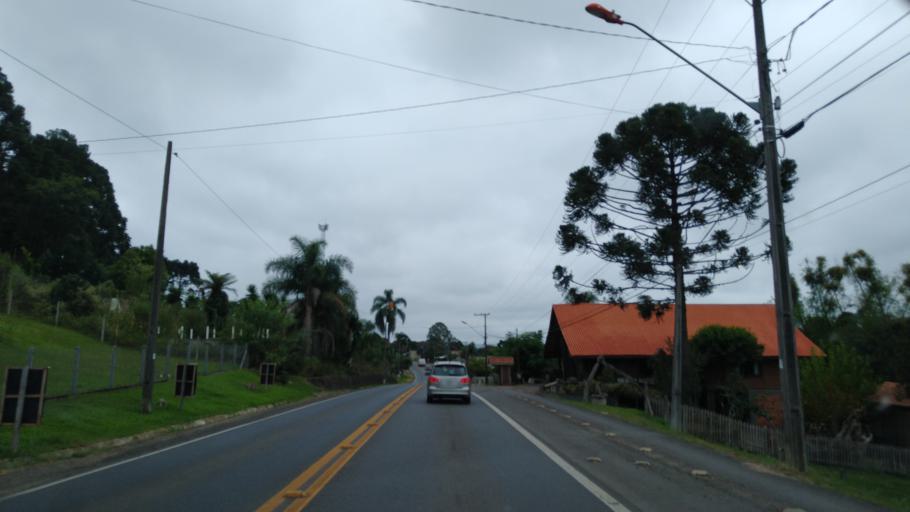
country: BR
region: Santa Catarina
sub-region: Porto Uniao
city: Porto Uniao
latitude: -26.2732
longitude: -51.0547
